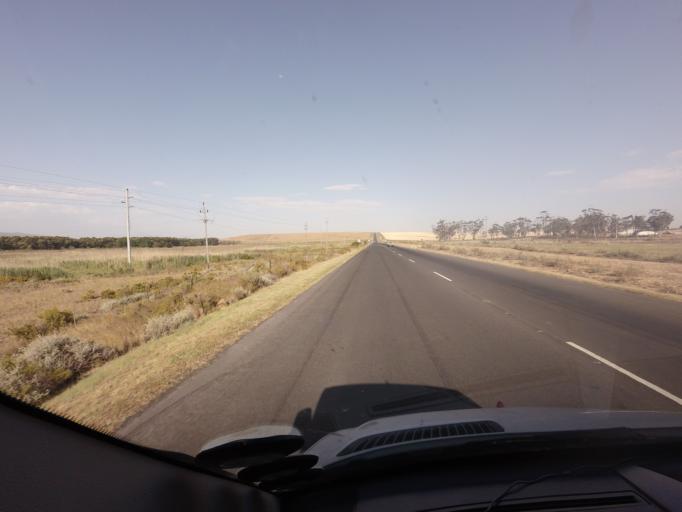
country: ZA
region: Western Cape
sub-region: Cape Winelands District Municipality
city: Ashton
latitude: -34.1556
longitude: 19.9385
